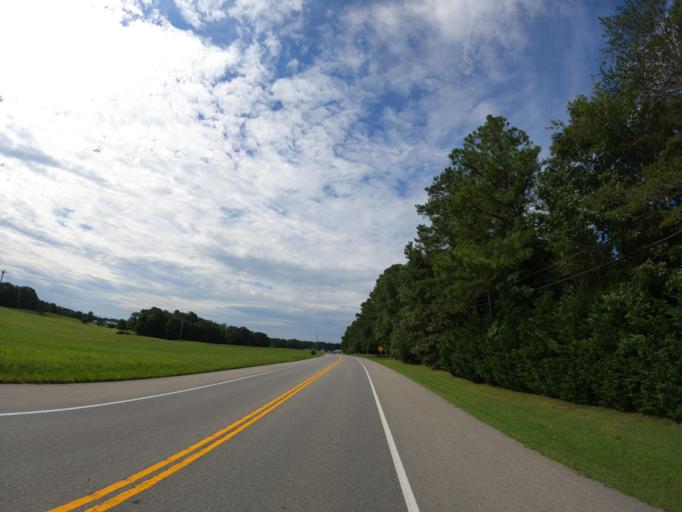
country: US
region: Maryland
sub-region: Saint Mary's County
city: Mechanicsville
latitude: 38.4052
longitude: -76.7216
